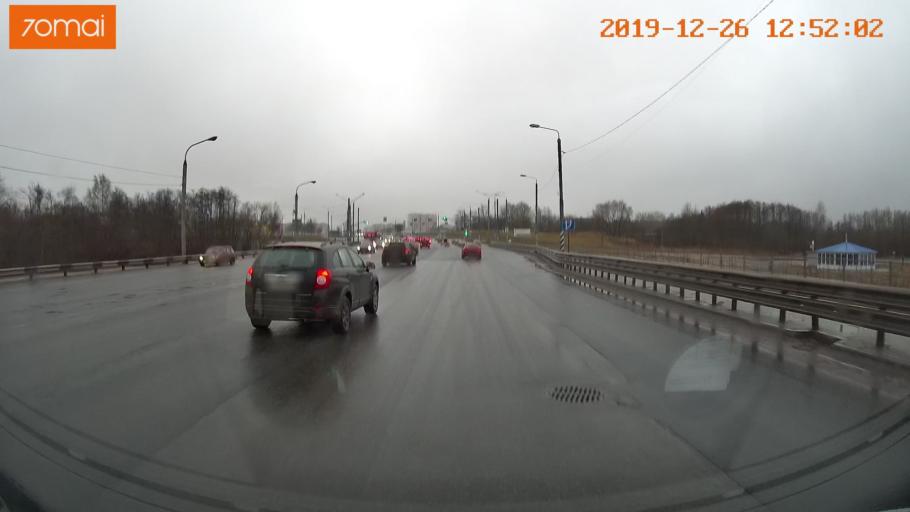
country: RU
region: Vologda
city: Cherepovets
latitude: 59.1072
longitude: 37.9050
